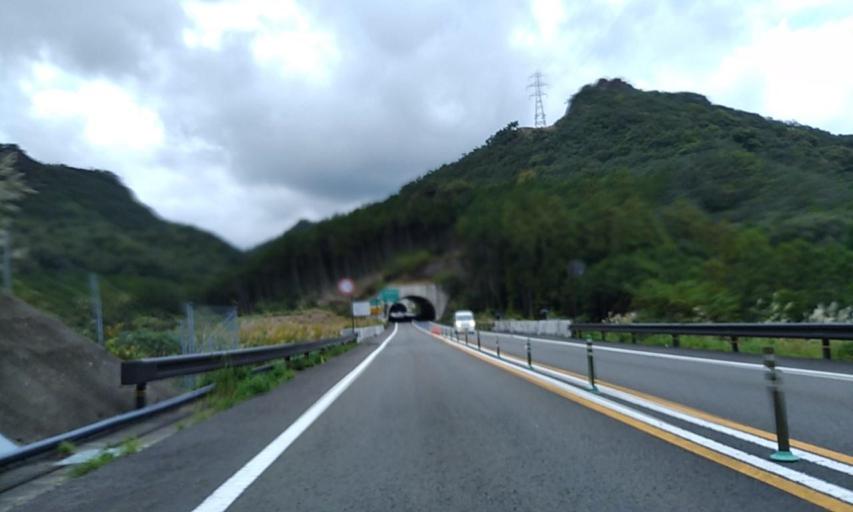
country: JP
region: Wakayama
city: Shingu
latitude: 33.6321
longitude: 135.9237
